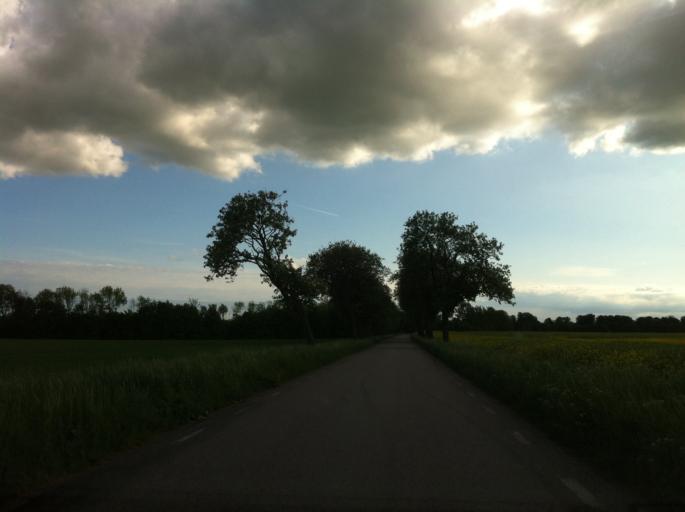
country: SE
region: Skane
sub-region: Svalovs Kommun
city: Kagerod
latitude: 56.0104
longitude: 13.0946
